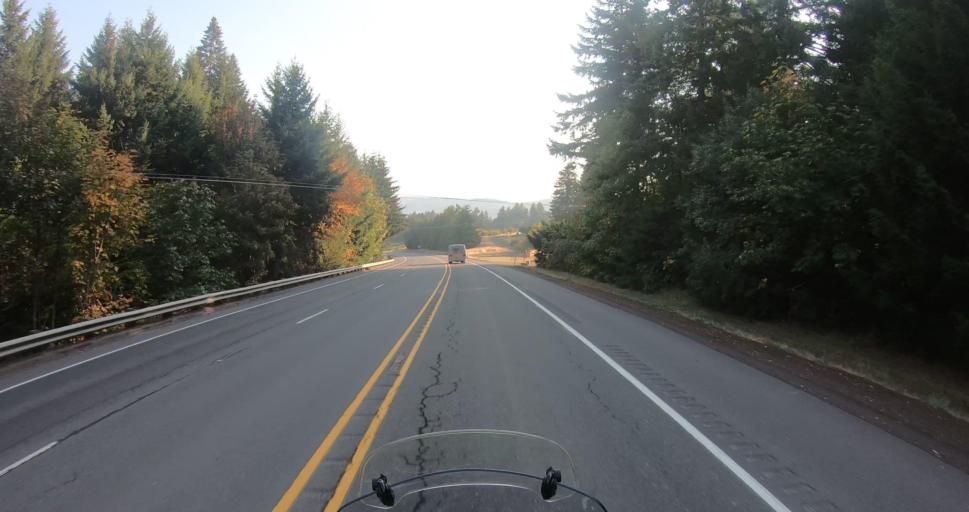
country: US
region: Oregon
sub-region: Hood River County
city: Odell
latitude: 45.6019
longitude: -121.5415
